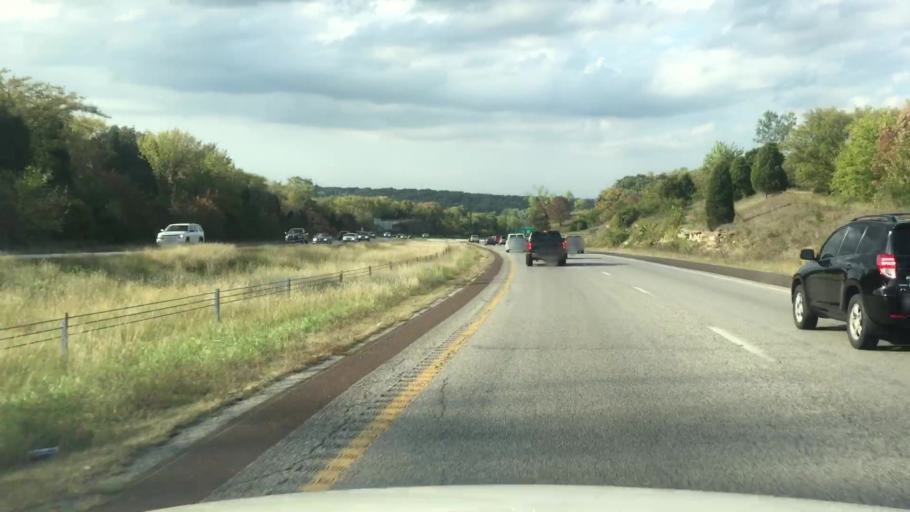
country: US
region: Missouri
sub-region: Jackson County
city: Blue Springs
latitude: 39.0152
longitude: -94.3572
